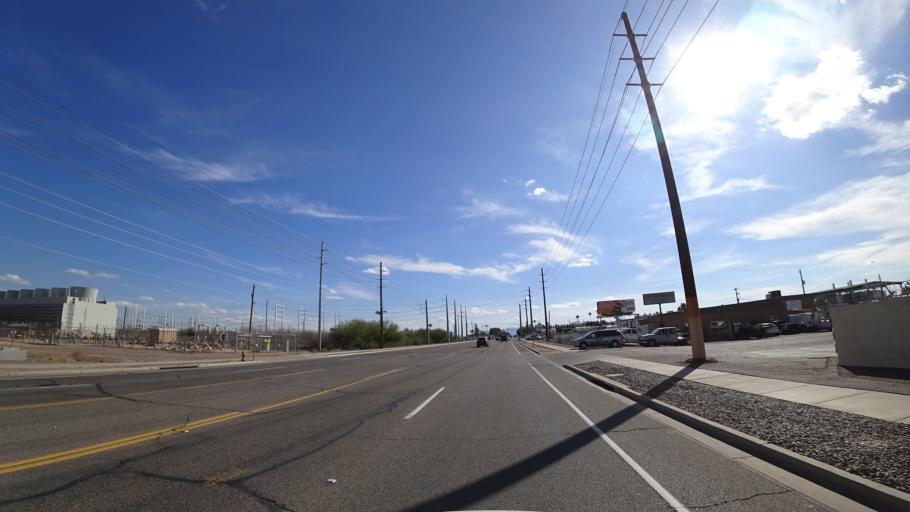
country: US
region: Arizona
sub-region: Maricopa County
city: Peoria
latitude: 33.5551
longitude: -112.2204
